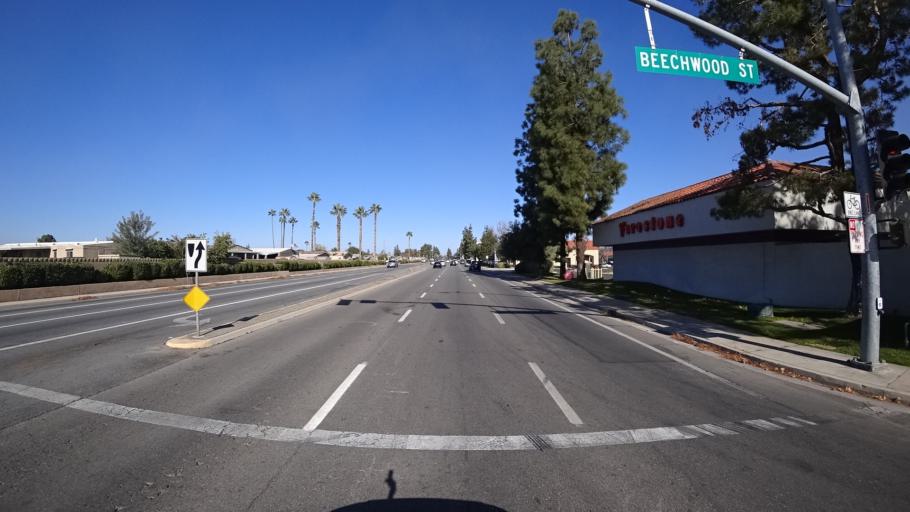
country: US
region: California
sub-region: Kern County
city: Bakersfield
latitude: 35.3215
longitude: -119.0566
